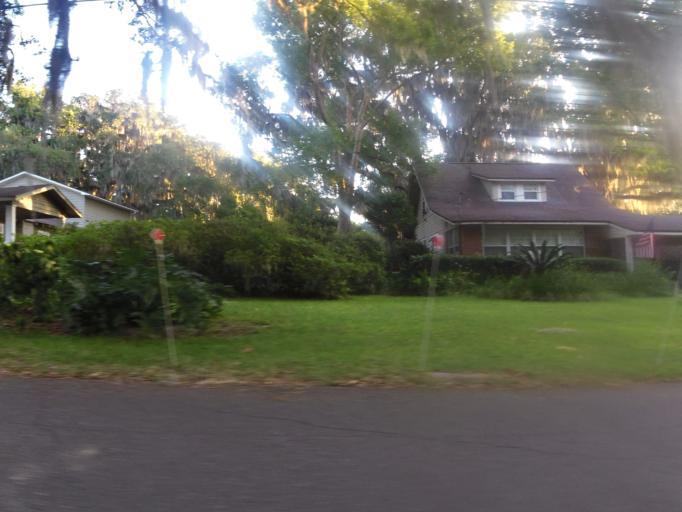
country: US
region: Florida
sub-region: Duval County
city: Jacksonville
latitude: 30.2707
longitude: -81.7101
